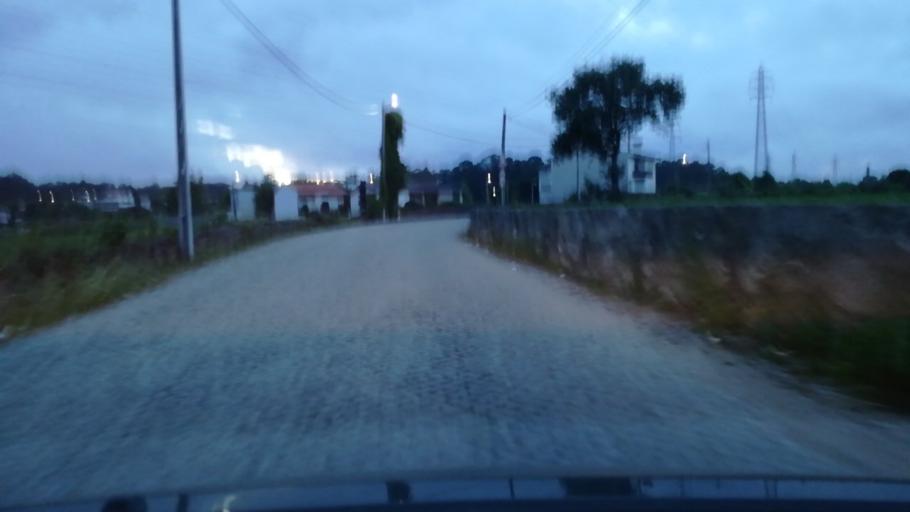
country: PT
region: Porto
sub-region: Maia
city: Maia
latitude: 41.2521
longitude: -8.6198
